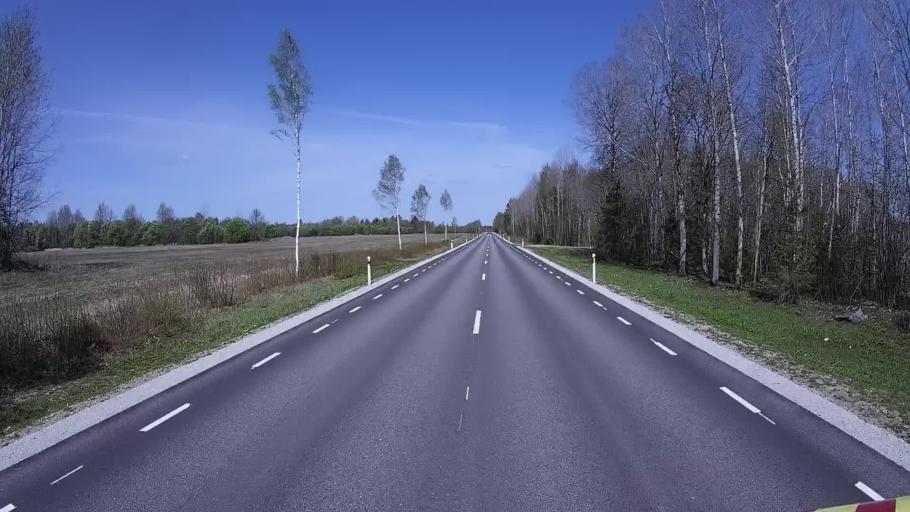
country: EE
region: Harju
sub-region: Nissi vald
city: Turba
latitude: 59.1592
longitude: 24.0741
